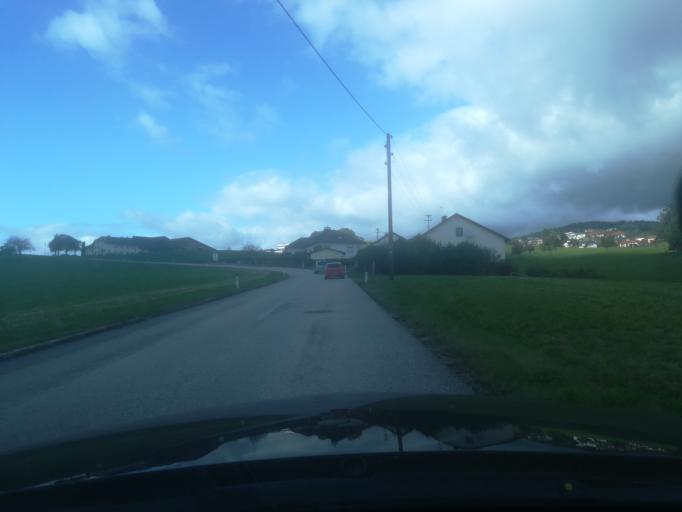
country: AT
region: Upper Austria
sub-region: Linz Stadt
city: Linz
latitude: 48.3517
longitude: 14.2635
